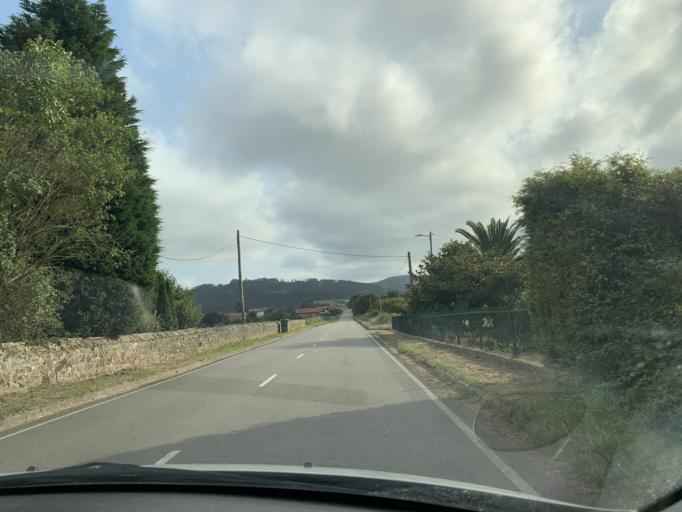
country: ES
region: Asturias
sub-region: Province of Asturias
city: Villaviciosa
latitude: 43.5334
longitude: -5.4278
